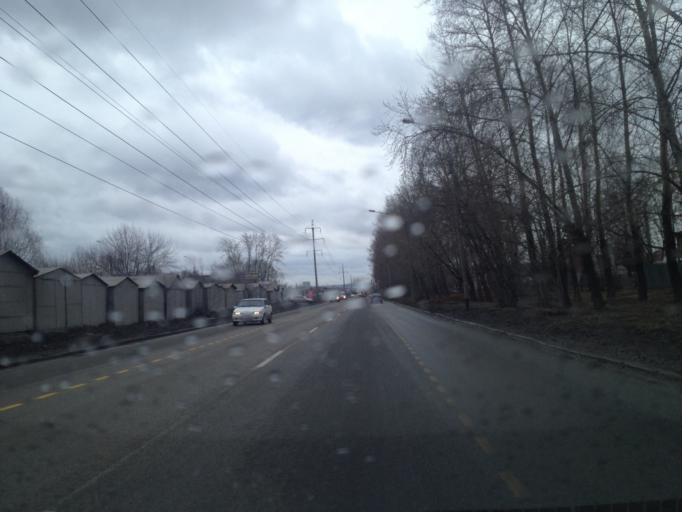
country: RU
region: Sverdlovsk
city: Sovkhoznyy
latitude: 56.7681
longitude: 60.5944
